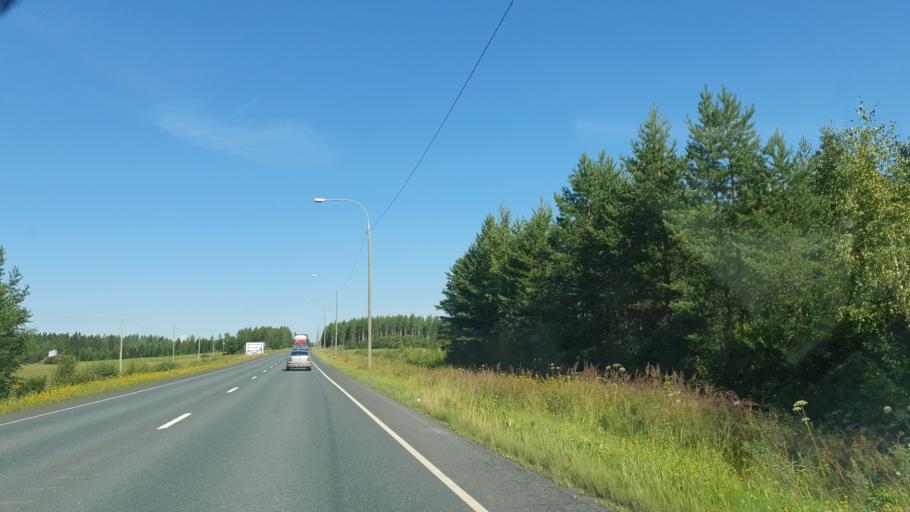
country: FI
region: Northern Savo
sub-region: Ylae-Savo
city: Lapinlahti
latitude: 63.3106
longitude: 27.4481
